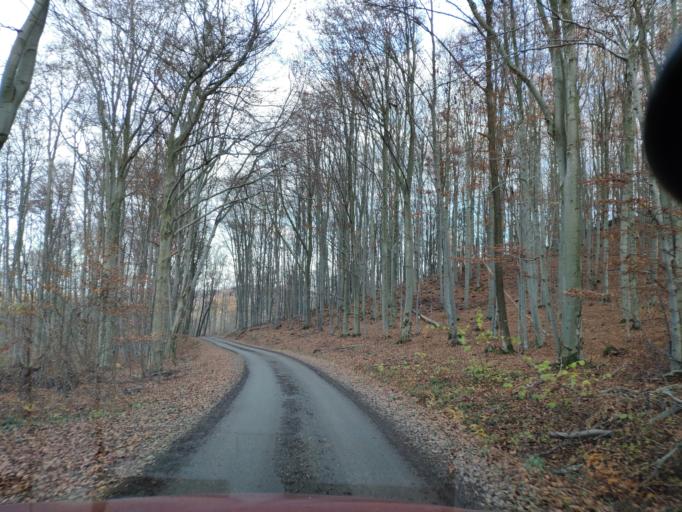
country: SK
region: Kosicky
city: Secovce
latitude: 48.5808
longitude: 21.4758
